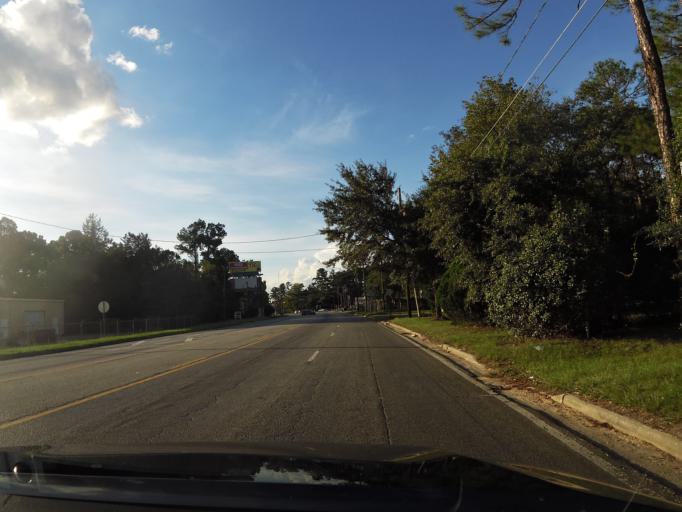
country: US
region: Georgia
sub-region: Lowndes County
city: Remerton
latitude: 30.8212
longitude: -83.3024
